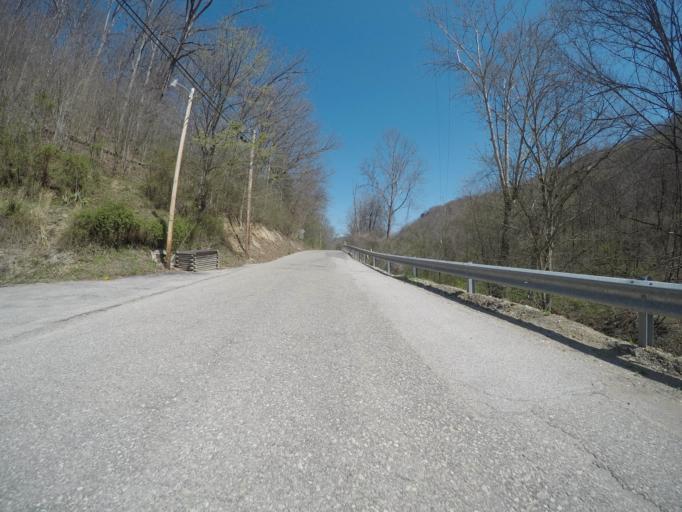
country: US
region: West Virginia
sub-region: Kanawha County
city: Pinch
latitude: 38.4131
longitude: -81.5583
